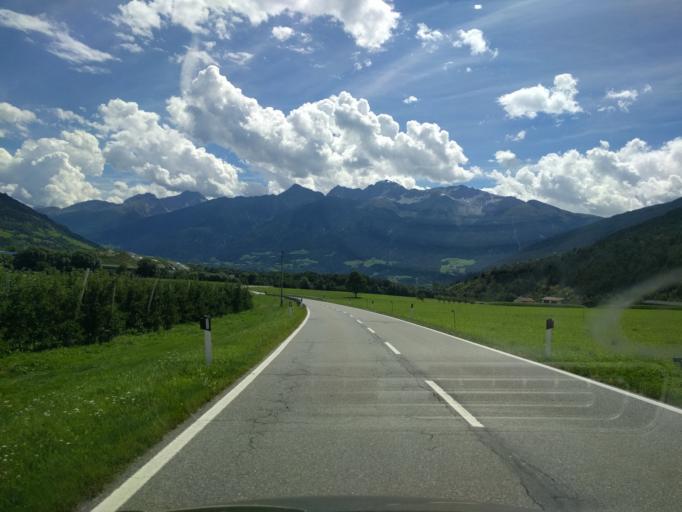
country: IT
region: Trentino-Alto Adige
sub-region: Bolzano
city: Glorenza
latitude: 46.6616
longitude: 10.5600
